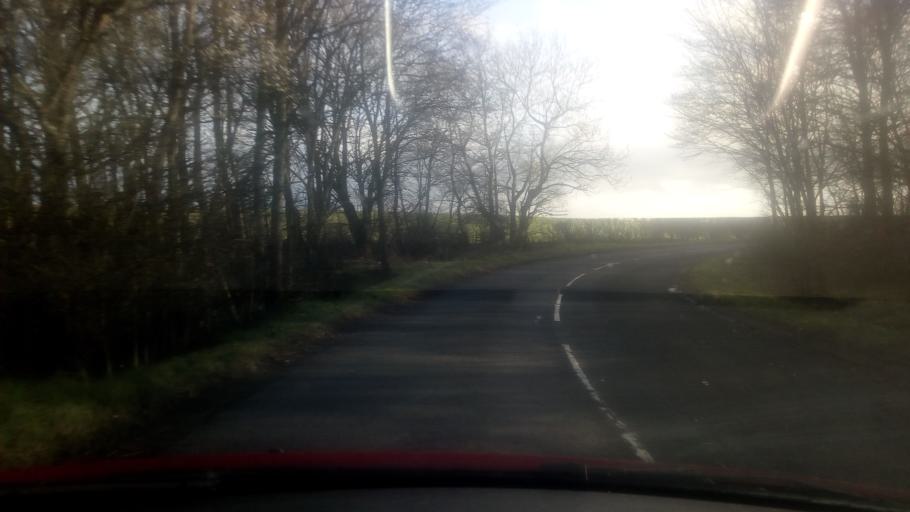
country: GB
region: Scotland
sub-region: The Scottish Borders
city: Kelso
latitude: 55.6410
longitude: -2.4056
